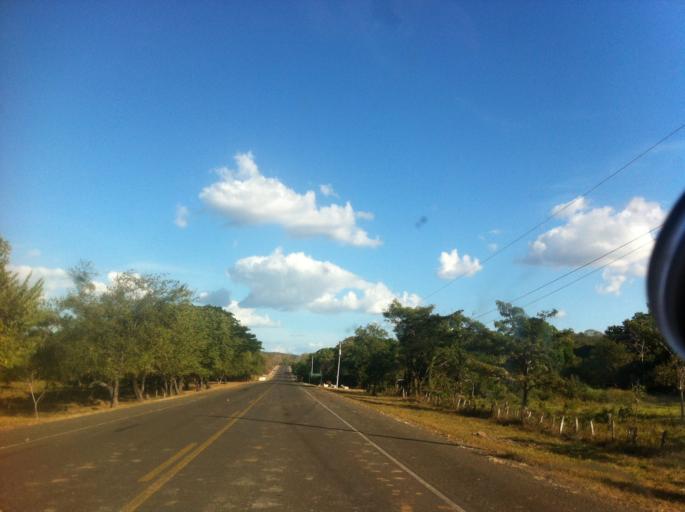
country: NI
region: Chontales
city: Acoyapa
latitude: 11.8951
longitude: -85.1176
